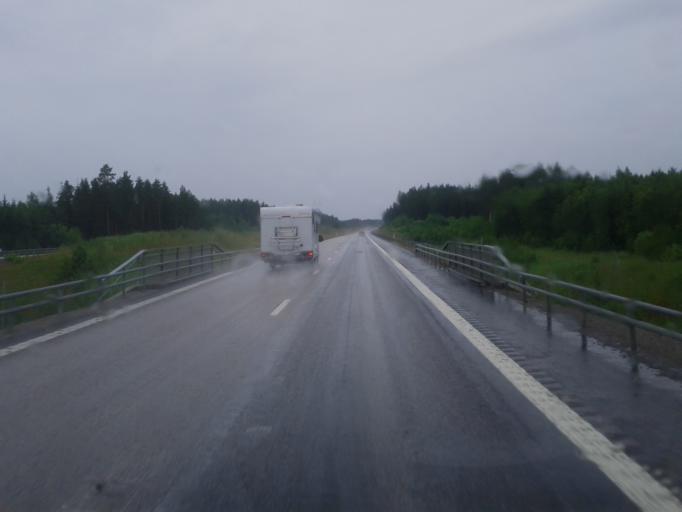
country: SE
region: Uppsala
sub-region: Tierps Kommun
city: Tierp
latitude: 60.2486
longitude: 17.5012
